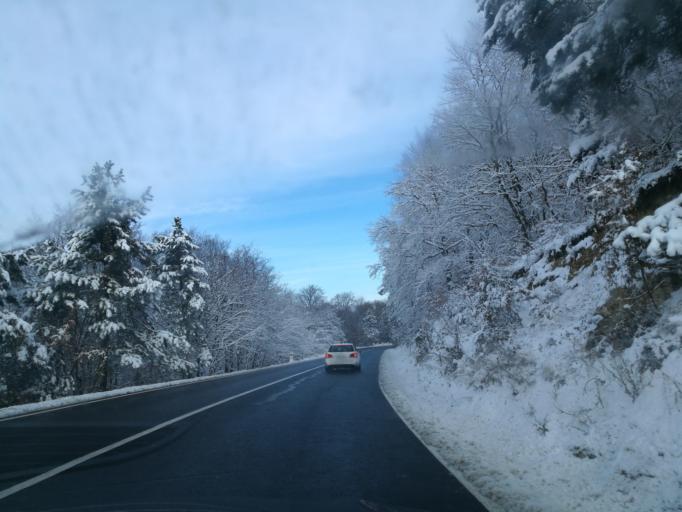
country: RO
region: Brasov
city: Brasov
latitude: 45.6409
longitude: 25.5615
